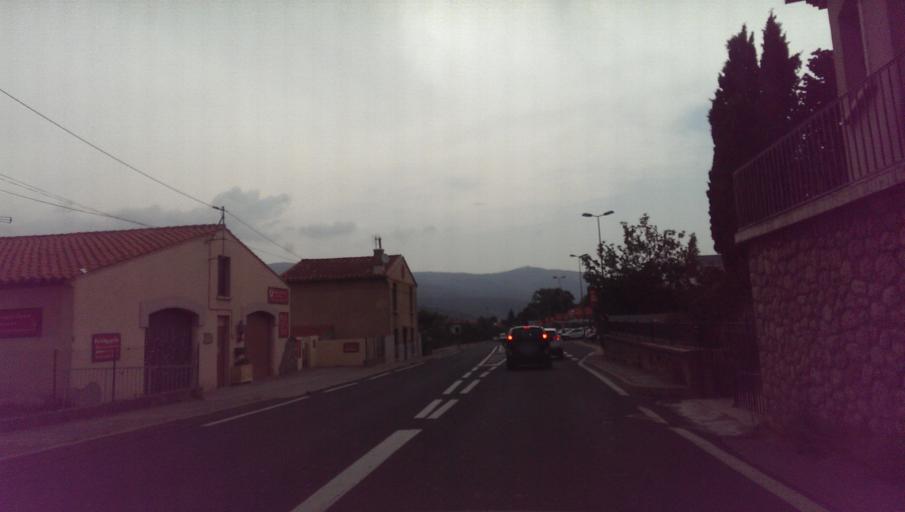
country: FR
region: Languedoc-Roussillon
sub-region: Departement des Pyrenees-Orientales
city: Ria-Sirach
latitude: 42.6121
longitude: 2.4100
